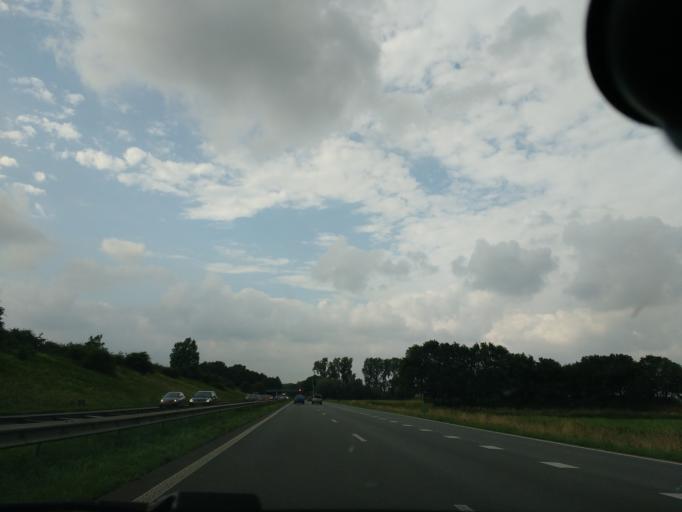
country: NL
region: Gelderland
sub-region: Gemeente Overbetuwe
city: Elst
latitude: 51.9354
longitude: 5.8778
